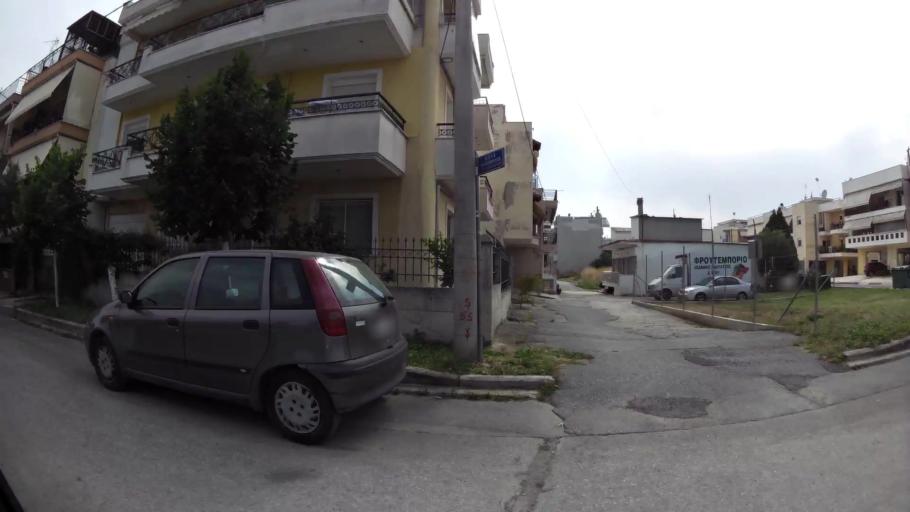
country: GR
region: Central Macedonia
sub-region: Nomos Thessalonikis
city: Stavroupoli
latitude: 40.6837
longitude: 22.9371
